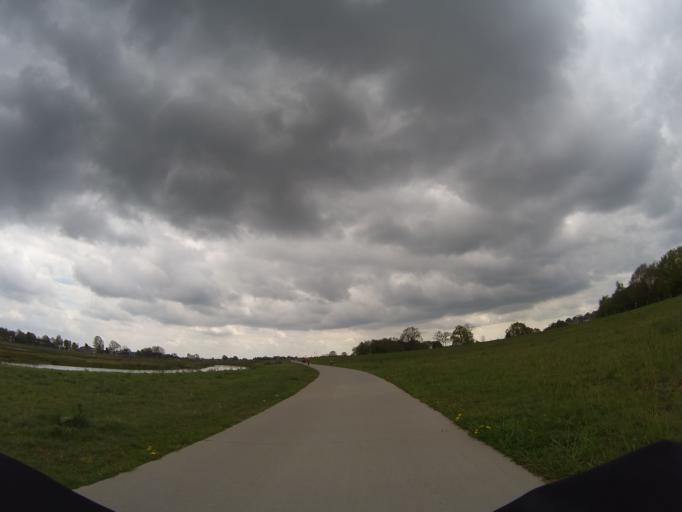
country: NL
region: Overijssel
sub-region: Gemeente Hardenberg
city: Hardenberg
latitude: 52.5687
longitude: 6.6118
